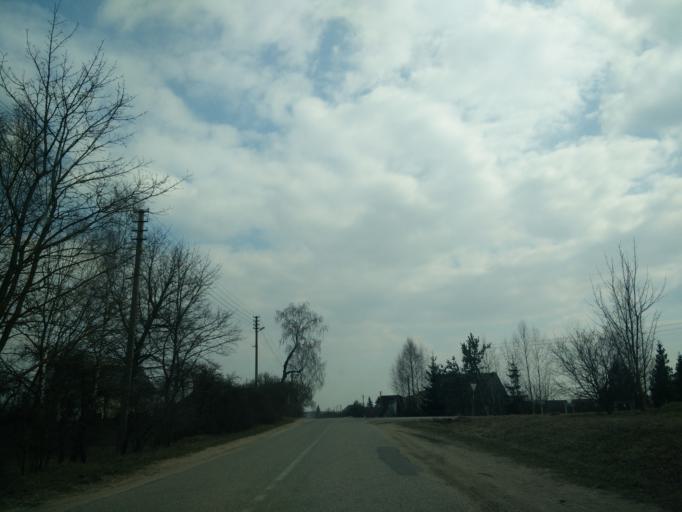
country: LT
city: Trakai
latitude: 54.6111
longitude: 24.9820
